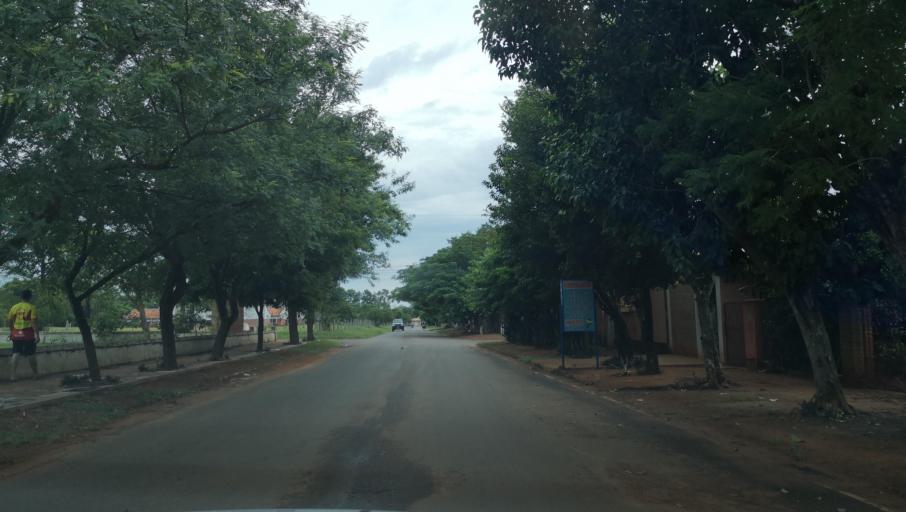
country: PY
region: Misiones
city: Santa Maria
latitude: -26.8880
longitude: -57.0405
